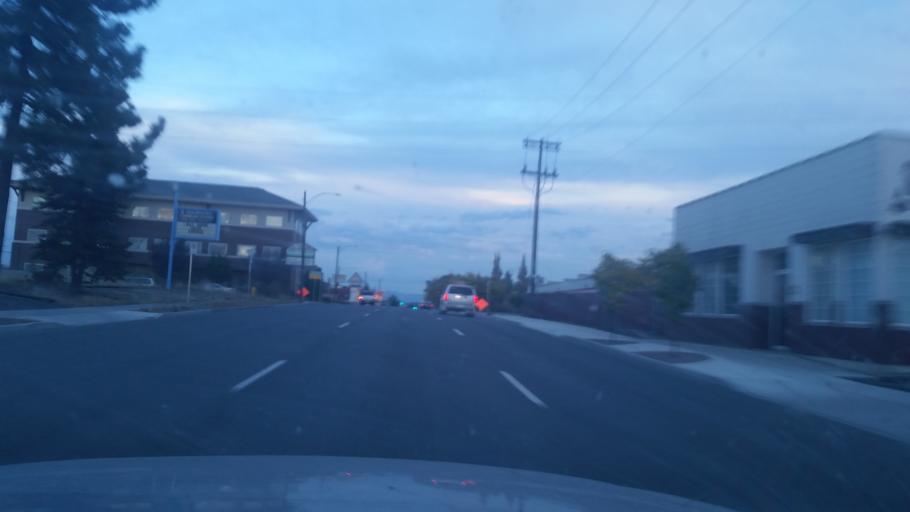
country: US
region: Washington
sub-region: Spokane County
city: Spokane
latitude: 47.6536
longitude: -117.4017
